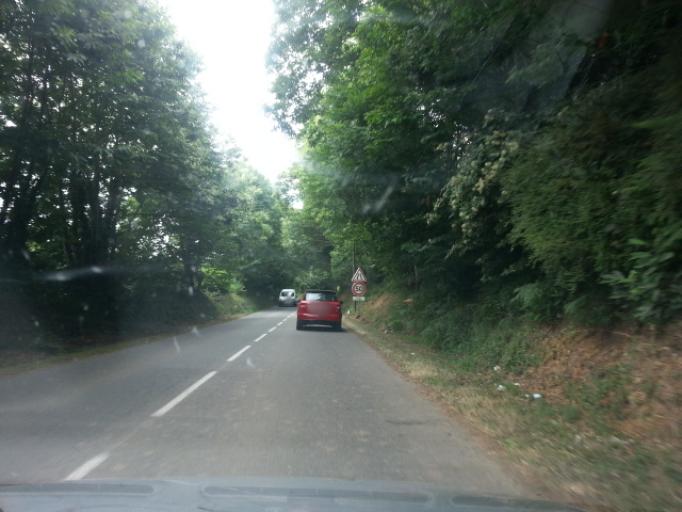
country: FR
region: Brittany
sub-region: Departement du Finistere
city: Melgven
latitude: 47.8851
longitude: -3.8238
